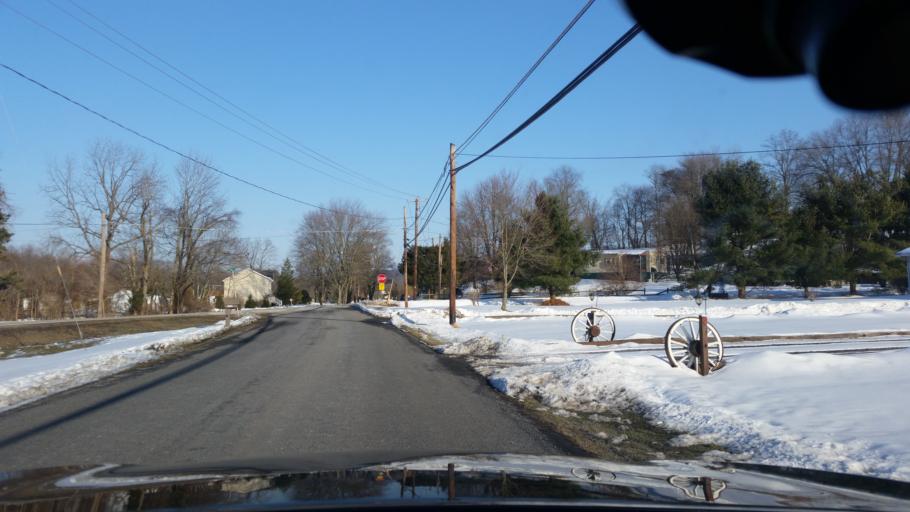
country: US
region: Pennsylvania
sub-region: Perry County
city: Duncannon
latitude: 40.3265
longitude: -77.0033
